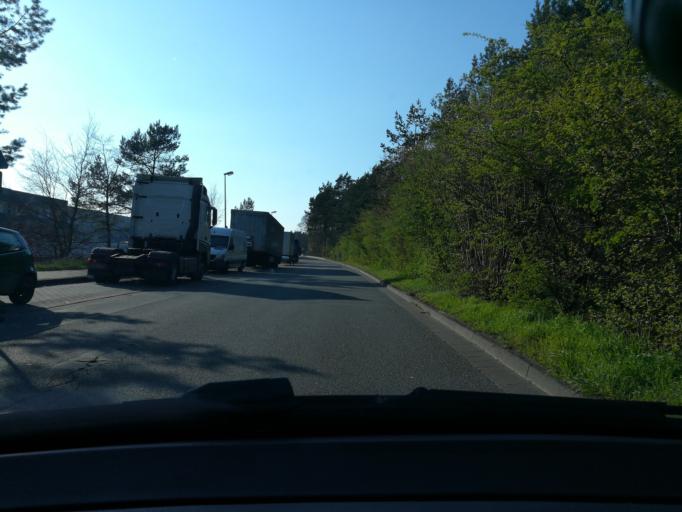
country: DE
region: North Rhine-Westphalia
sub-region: Regierungsbezirk Detmold
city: Verl
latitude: 51.9444
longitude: 8.5652
